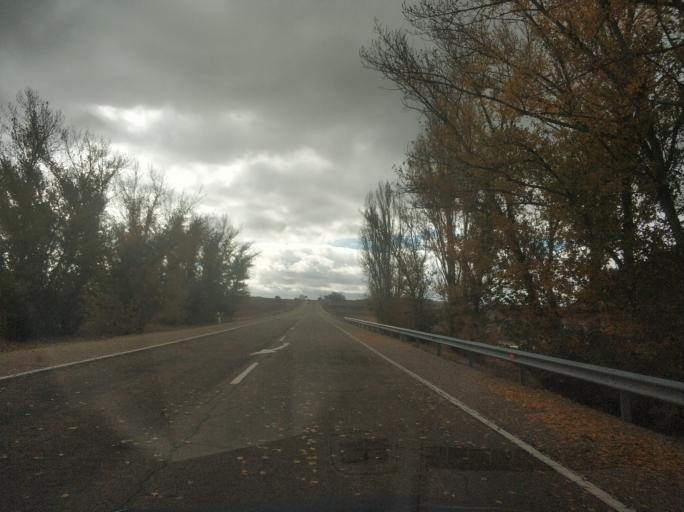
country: ES
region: Castille and Leon
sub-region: Provincia de Zamora
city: Castrillo de la Guarena
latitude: 41.2282
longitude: -5.3120
